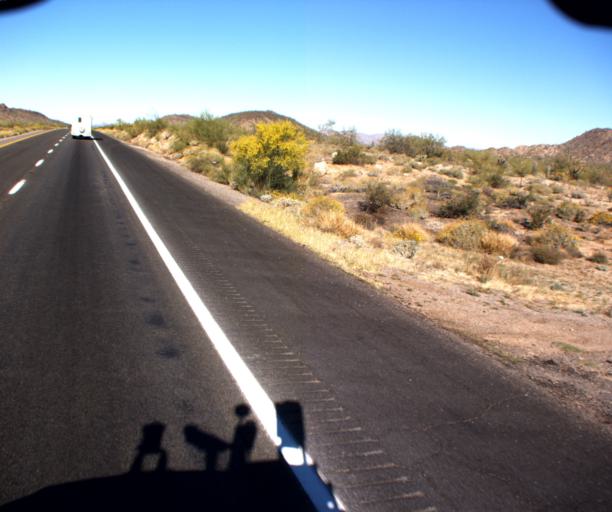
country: US
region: Arizona
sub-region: Pinal County
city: Maricopa
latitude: 32.8352
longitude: -112.1587
